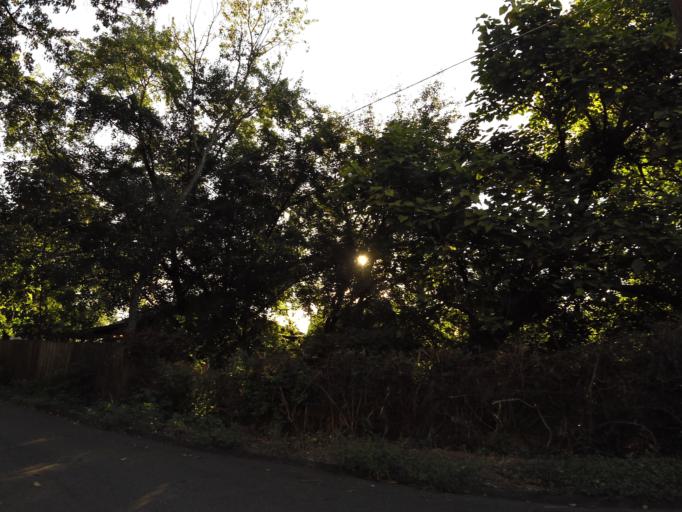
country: US
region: Tennessee
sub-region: Knox County
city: Knoxville
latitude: 35.9744
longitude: -83.9384
